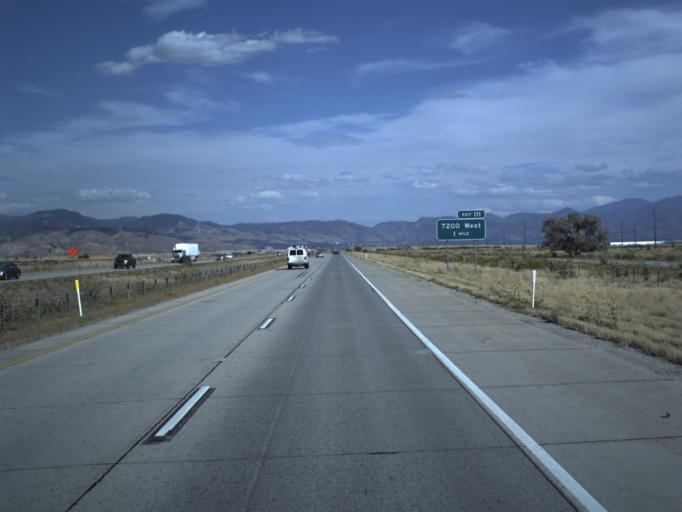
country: US
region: Utah
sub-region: Salt Lake County
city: Magna
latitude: 40.7708
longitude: -112.0903
